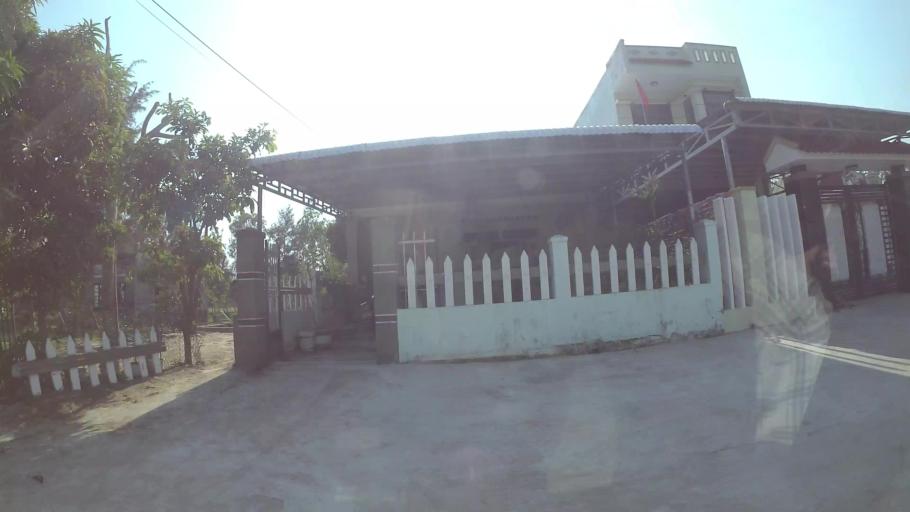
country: VN
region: Quang Nam
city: Quang Nam
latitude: 15.9516
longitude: 108.2666
